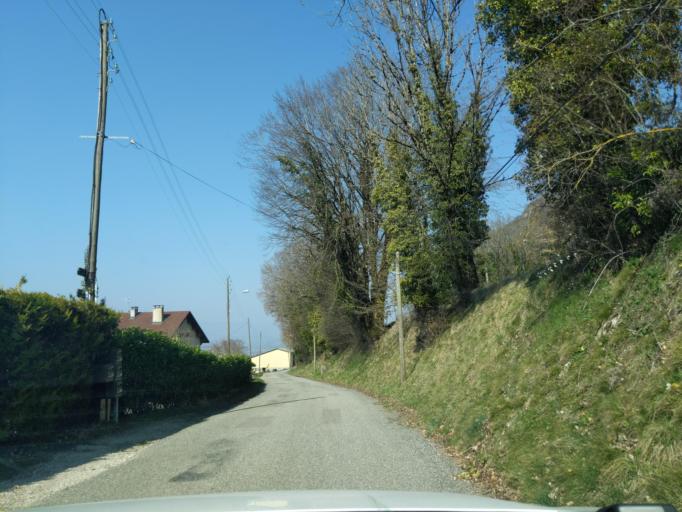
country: FR
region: Rhone-Alpes
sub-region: Departement de la Haute-Savoie
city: Moye
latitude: 45.9125
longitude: 5.8488
